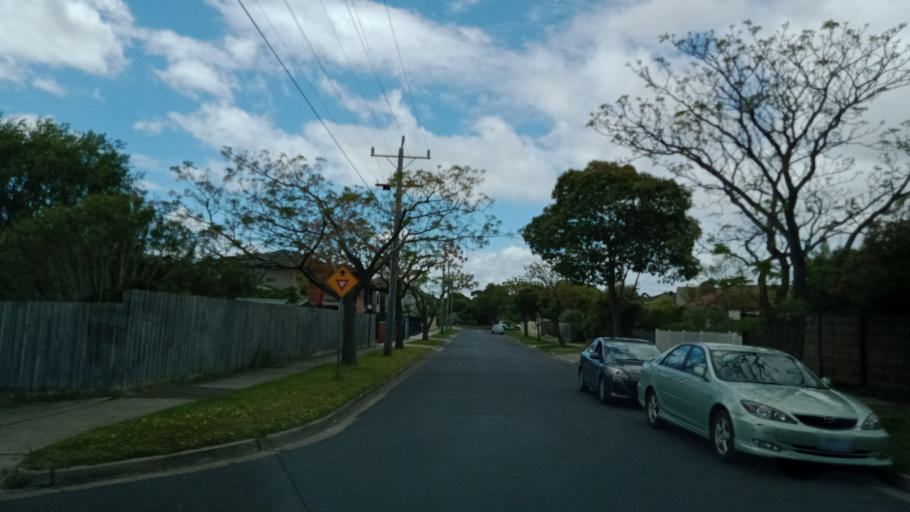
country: AU
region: Victoria
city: McKinnon
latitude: -37.9167
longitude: 145.0536
